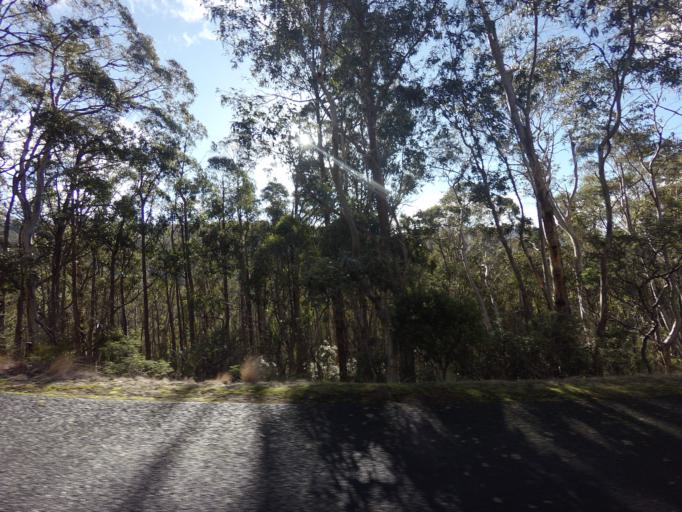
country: AU
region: Tasmania
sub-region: Glenorchy
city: Berriedale
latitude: -42.8364
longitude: 147.1708
